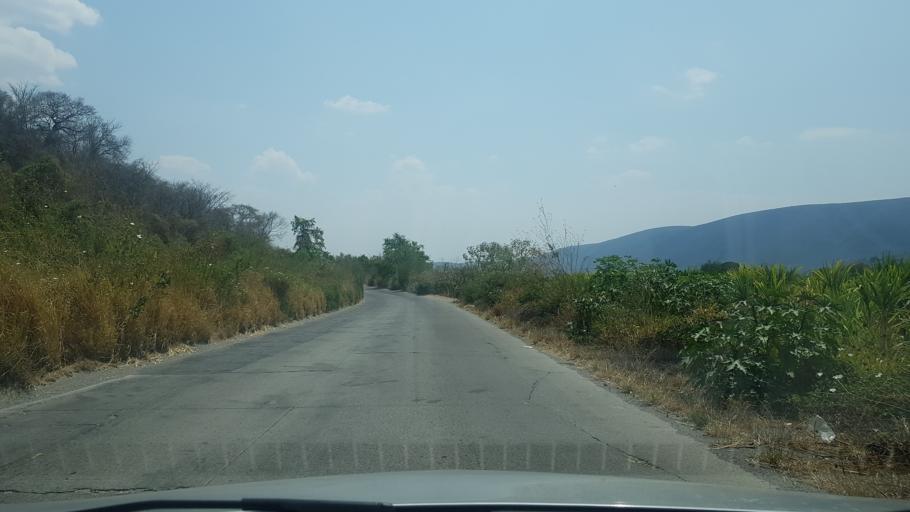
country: MX
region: Morelos
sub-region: Tlaltizapan de Zapata
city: Colonia Palo Prieto (Chipitongo)
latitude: 18.7743
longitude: -99.1075
